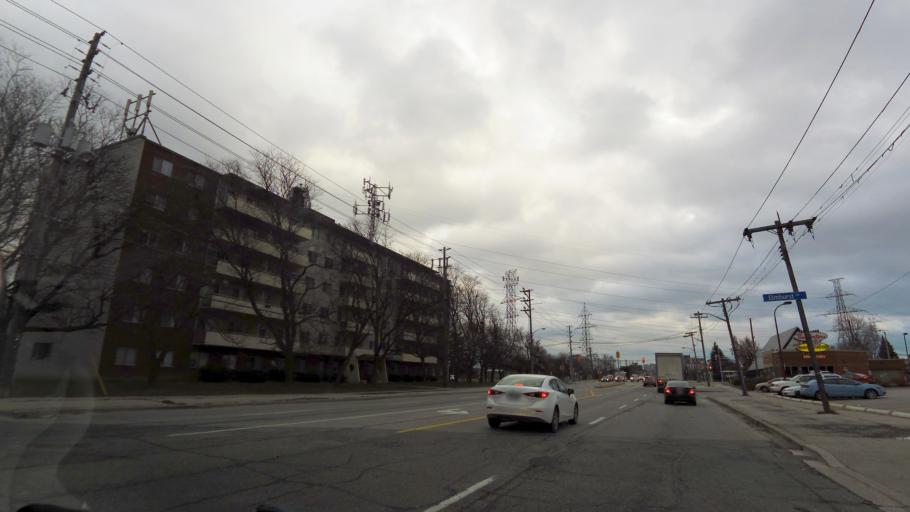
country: CA
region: Ontario
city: Etobicoke
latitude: 43.7241
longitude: -79.5594
